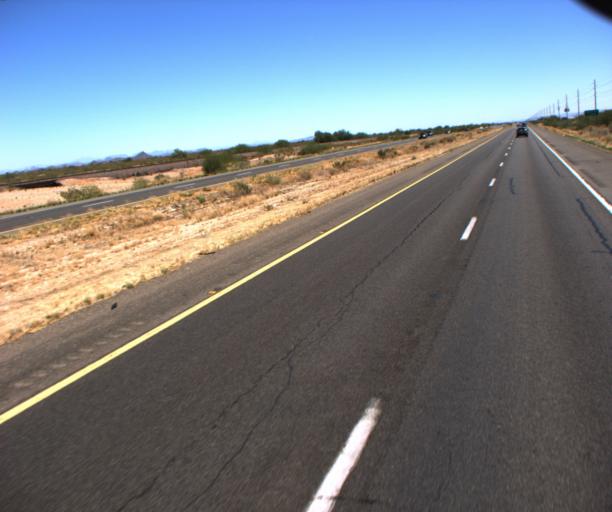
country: US
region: Arizona
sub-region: Maricopa County
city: Sun City West
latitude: 33.7436
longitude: -112.4849
